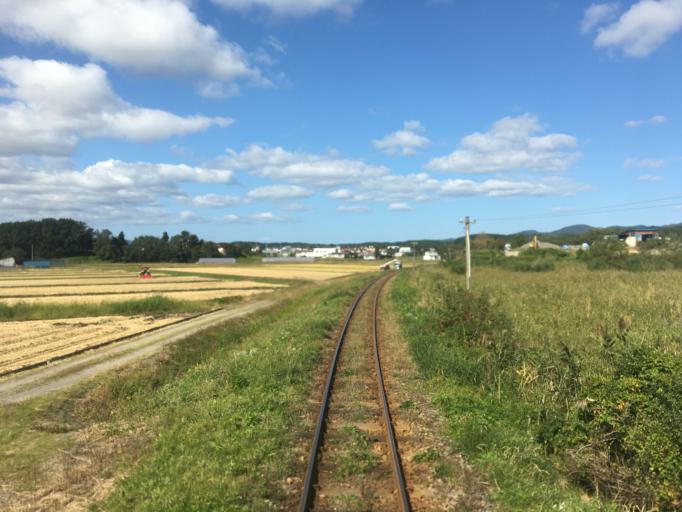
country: JP
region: Aomori
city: Goshogawara
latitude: 40.9476
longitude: 140.4379
